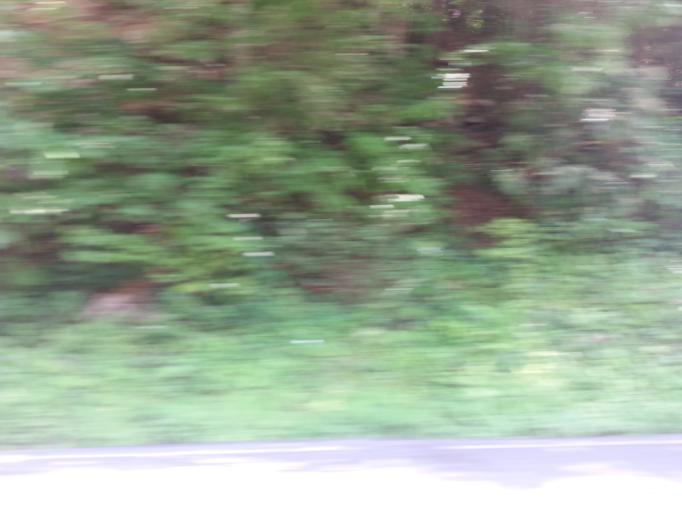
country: US
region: Virginia
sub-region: Lee County
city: Jonesville
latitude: 36.7667
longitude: -83.1081
